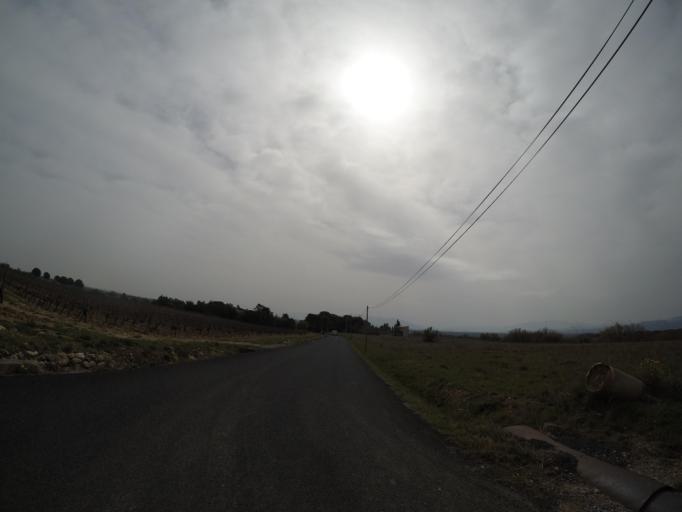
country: FR
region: Languedoc-Roussillon
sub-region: Departement des Pyrenees-Orientales
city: Pezilla-la-Riviere
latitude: 42.7079
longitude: 2.7594
